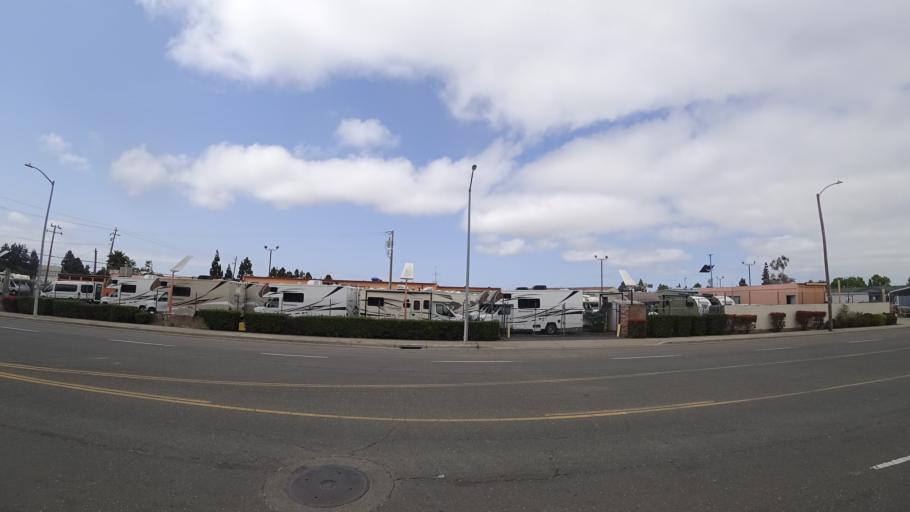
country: US
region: California
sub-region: Alameda County
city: Union City
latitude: 37.6223
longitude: -122.0576
